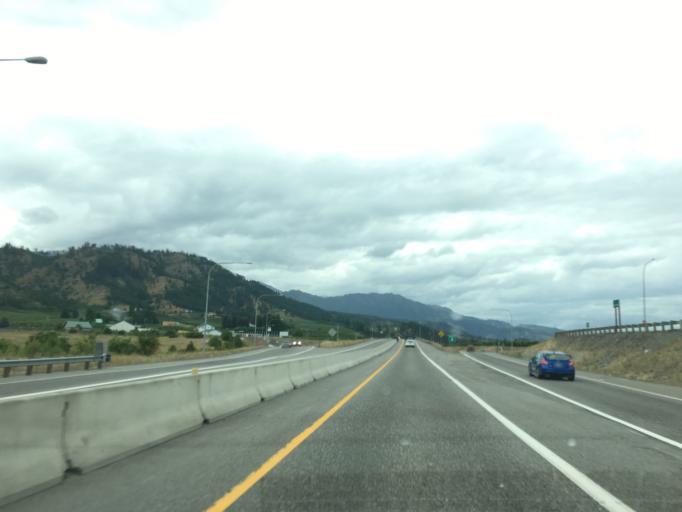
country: US
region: Washington
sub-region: Chelan County
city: Leavenworth
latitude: 47.5569
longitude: -120.5890
